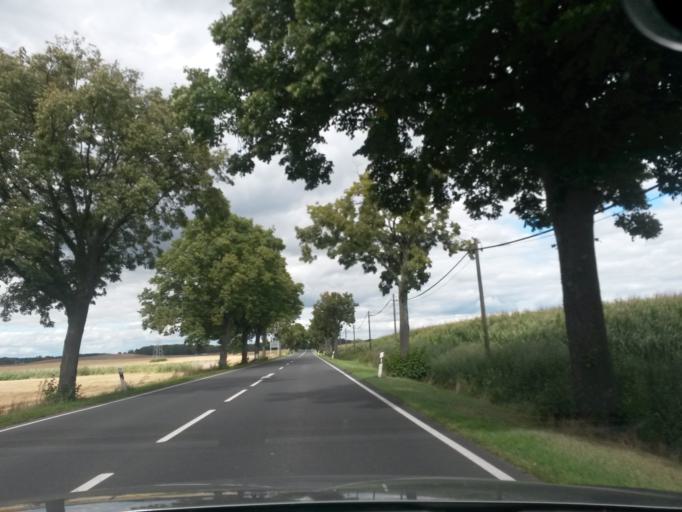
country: DE
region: Brandenburg
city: Angermunde
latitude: 52.9799
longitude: 13.9728
